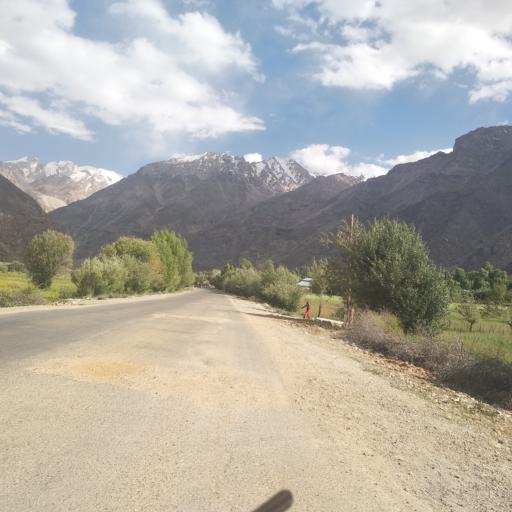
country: TJ
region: Gorno-Badakhshan
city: Roshtqal'a
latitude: 37.7270
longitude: 72.1600
